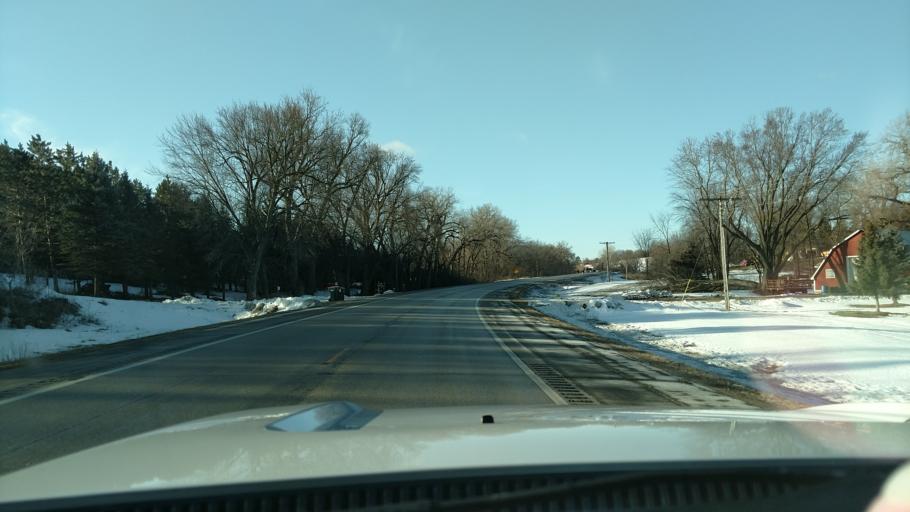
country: US
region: Minnesota
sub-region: Olmsted County
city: Rochester
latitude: 44.1230
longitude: -92.4206
